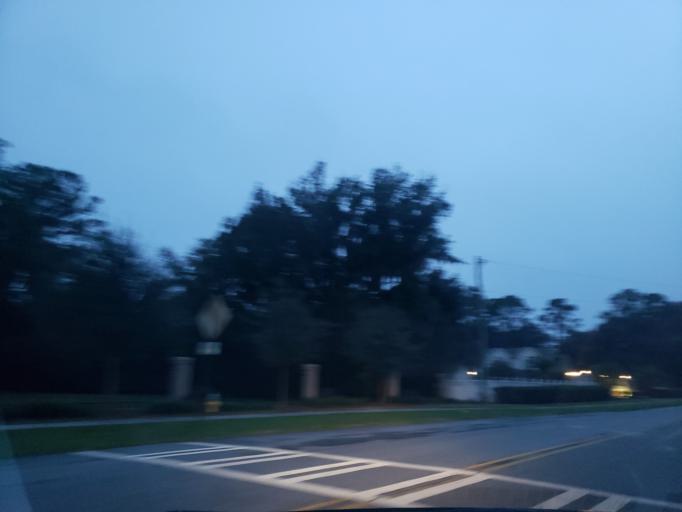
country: US
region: Georgia
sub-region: Chatham County
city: Wilmington Island
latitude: 32.0200
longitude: -80.9633
